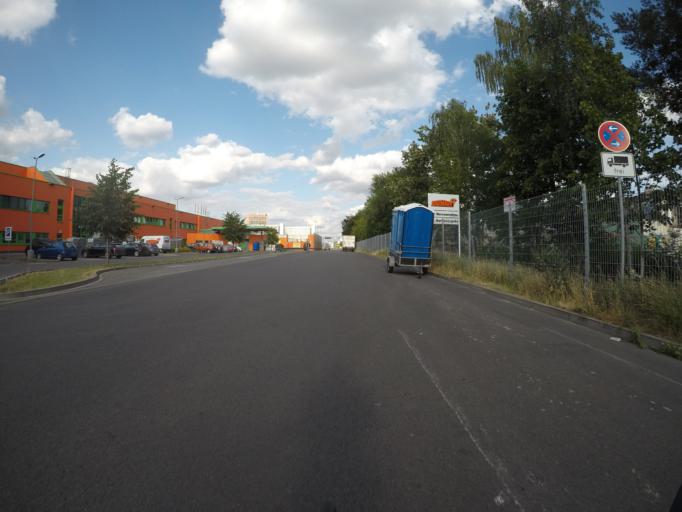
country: DE
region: Berlin
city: Alt-Hohenschoenhausen
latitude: 52.5321
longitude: 13.5088
